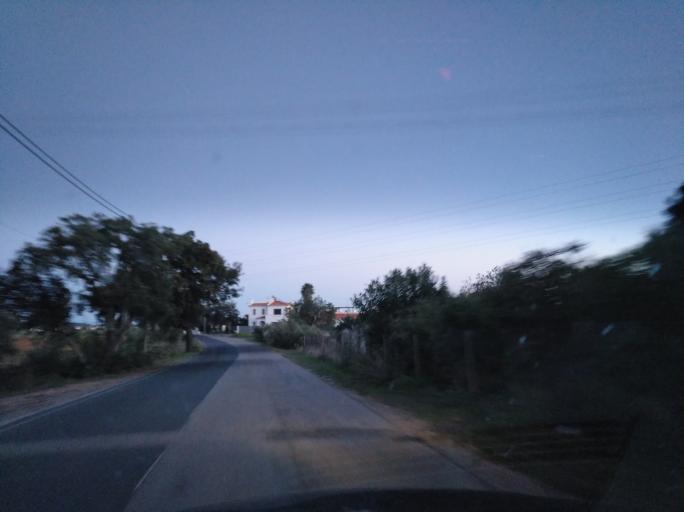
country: PT
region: Faro
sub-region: Vila Real de Santo Antonio
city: Monte Gordo
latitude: 37.1901
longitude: -7.5122
